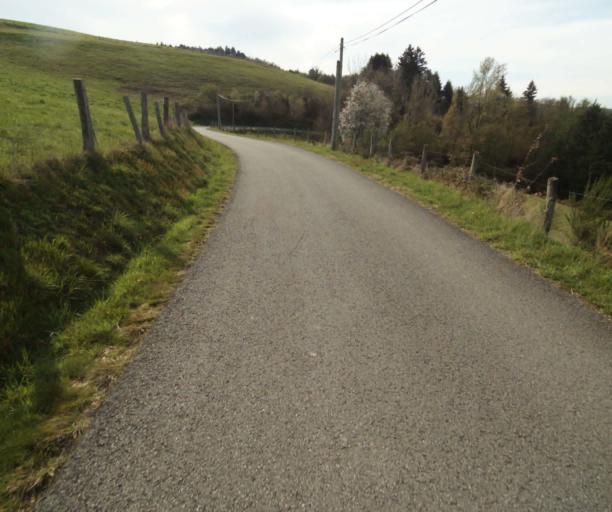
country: FR
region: Limousin
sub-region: Departement de la Correze
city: Correze
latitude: 45.3357
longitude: 1.8287
